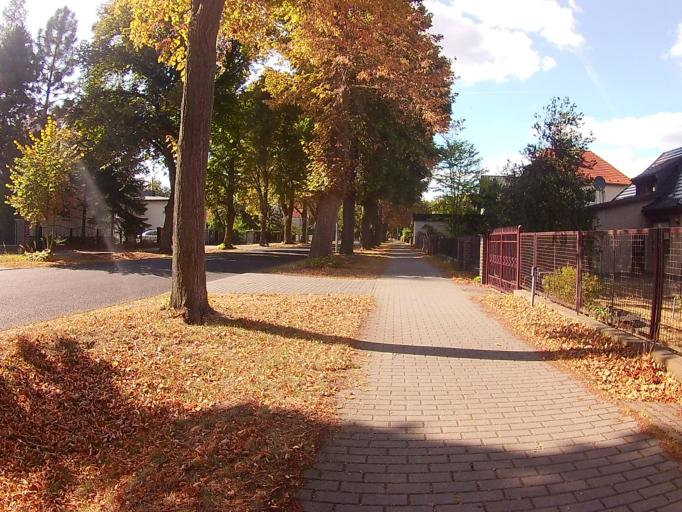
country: DE
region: Brandenburg
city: Zeuthen
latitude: 52.3706
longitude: 13.6042
